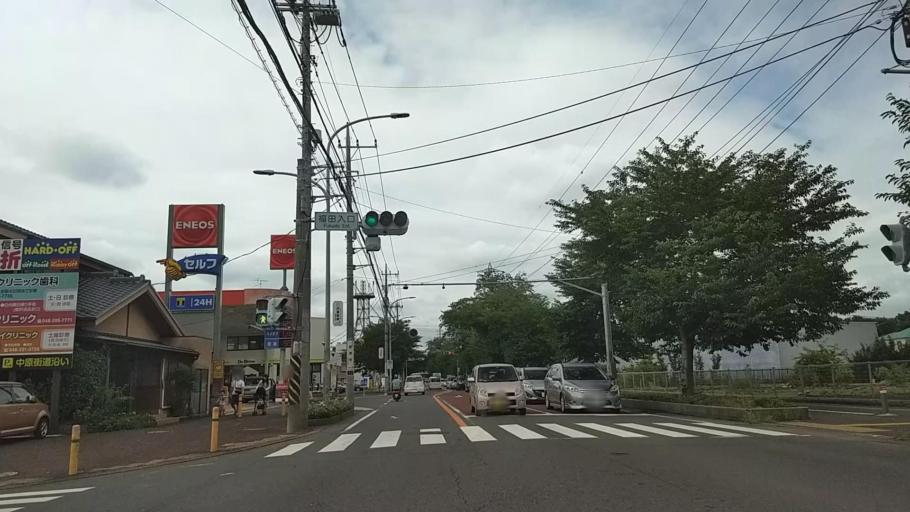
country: JP
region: Kanagawa
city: Minami-rinkan
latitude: 35.4363
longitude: 139.4669
